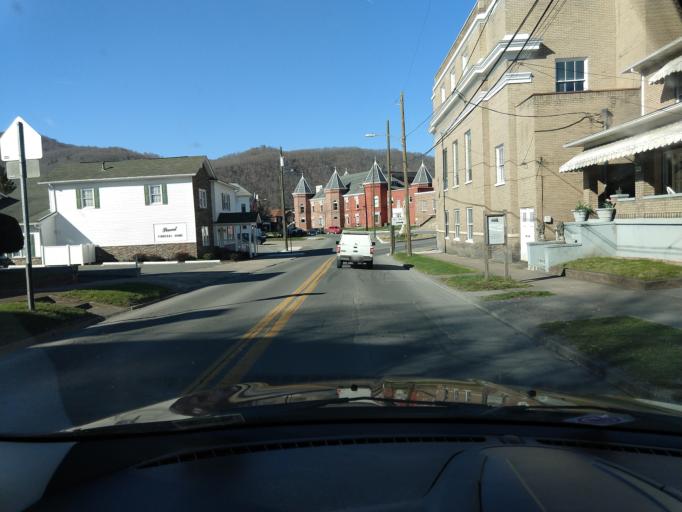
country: US
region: West Virginia
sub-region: Summers County
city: Hinton
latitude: 37.6725
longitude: -80.8906
